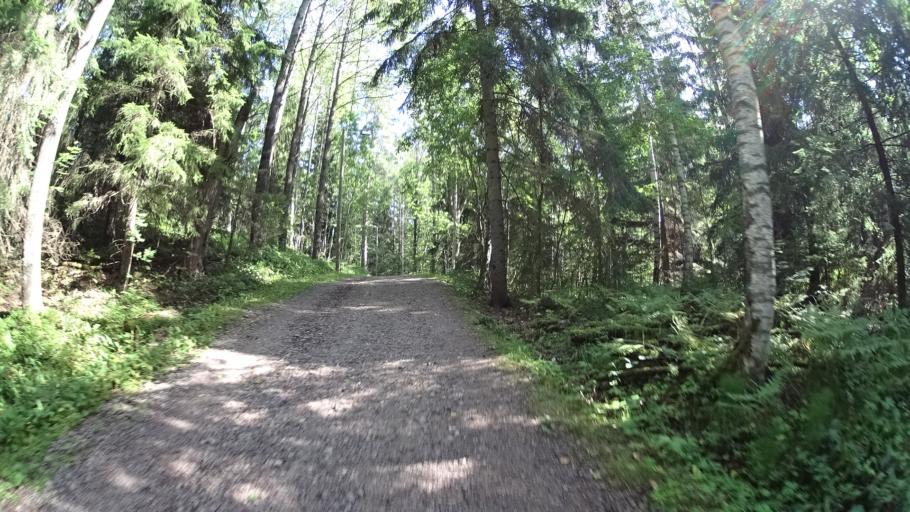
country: FI
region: Uusimaa
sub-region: Helsinki
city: Espoo
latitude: 60.2345
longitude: 24.6447
